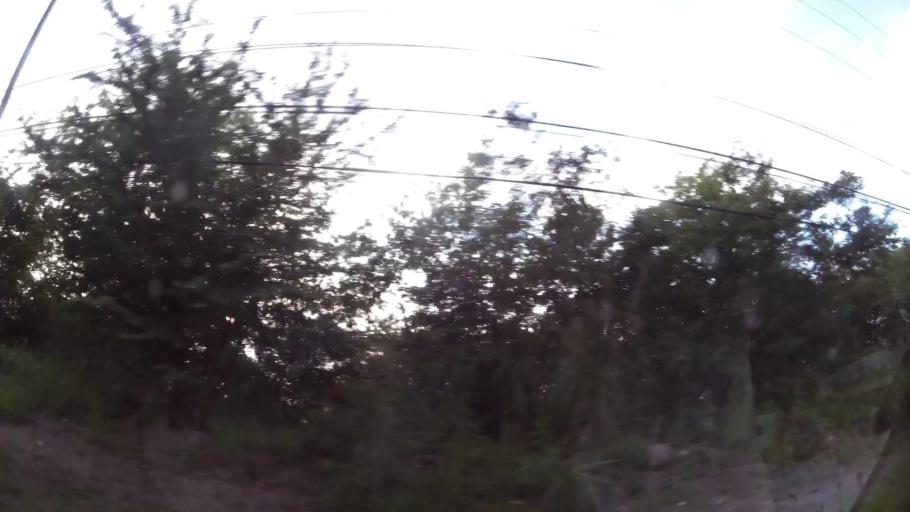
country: DM
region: Saint Joseph
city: Saint Joseph
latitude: 15.4010
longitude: -61.4270
